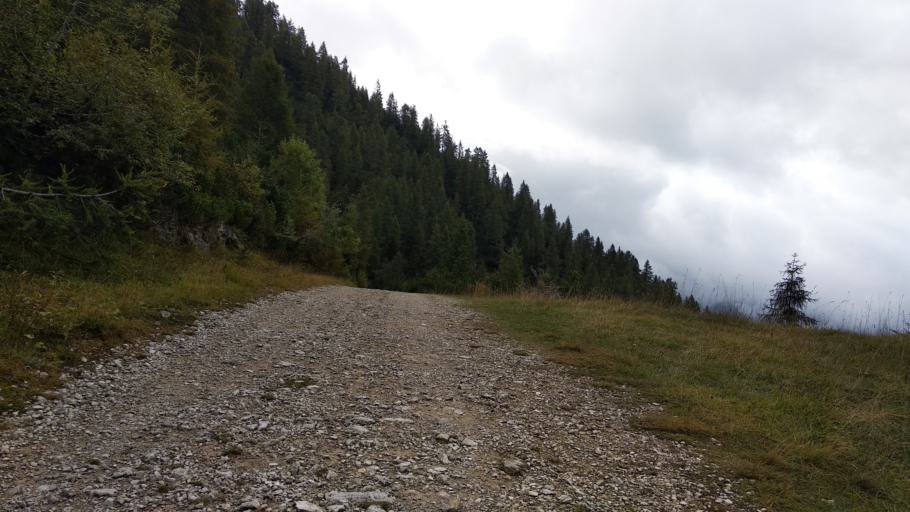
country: IT
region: Trentino-Alto Adige
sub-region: Provincia di Trento
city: Borgo
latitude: 45.9743
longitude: 11.4374
